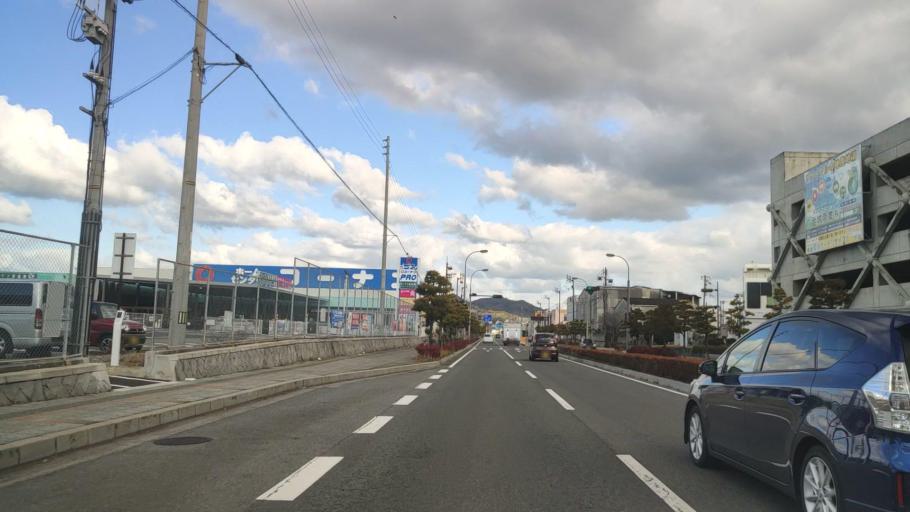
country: JP
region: Ehime
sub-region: Shikoku-chuo Shi
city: Matsuyama
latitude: 33.8507
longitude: 132.7132
